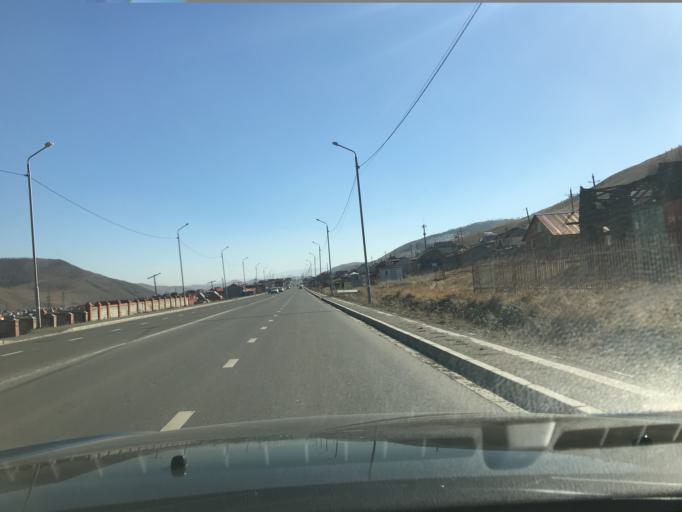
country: MN
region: Ulaanbaatar
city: Ulaanbaatar
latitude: 48.0470
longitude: 106.9011
